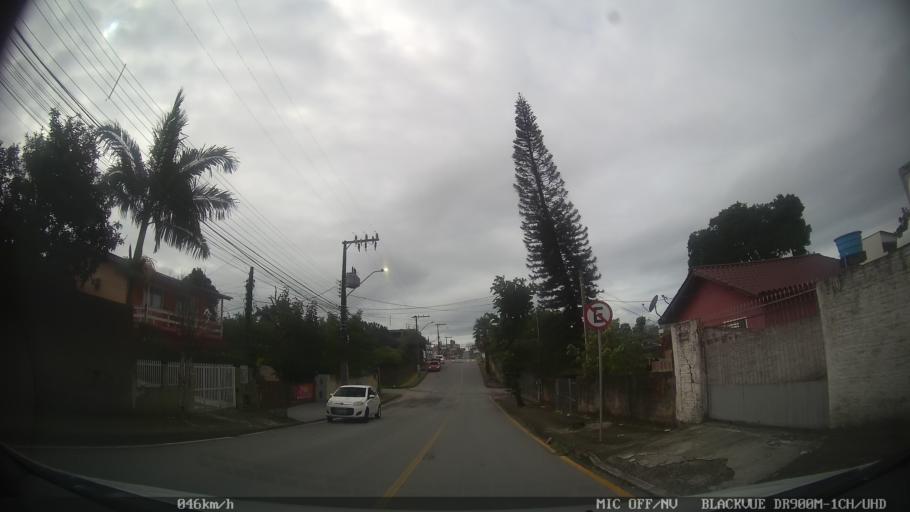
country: BR
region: Santa Catarina
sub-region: Biguacu
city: Biguacu
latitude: -27.5451
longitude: -48.6447
